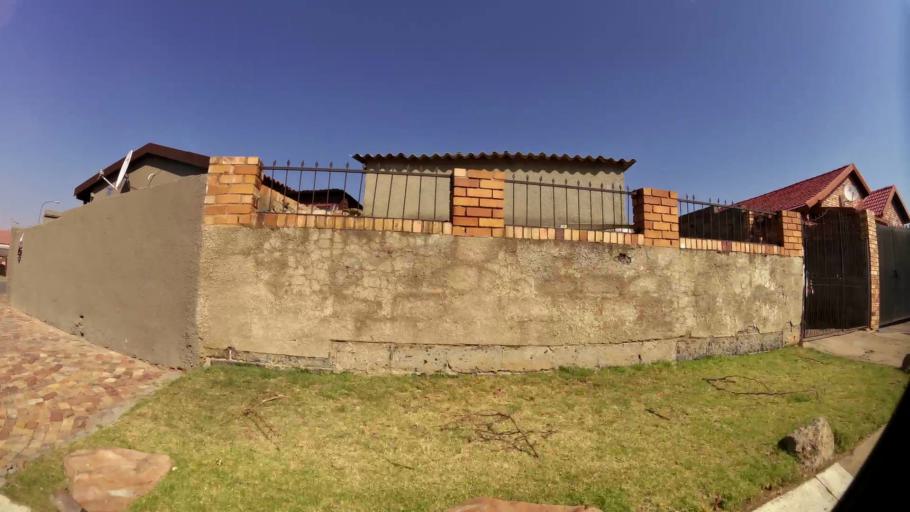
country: ZA
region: Gauteng
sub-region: City of Johannesburg Metropolitan Municipality
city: Johannesburg
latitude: -26.2450
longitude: 27.9616
